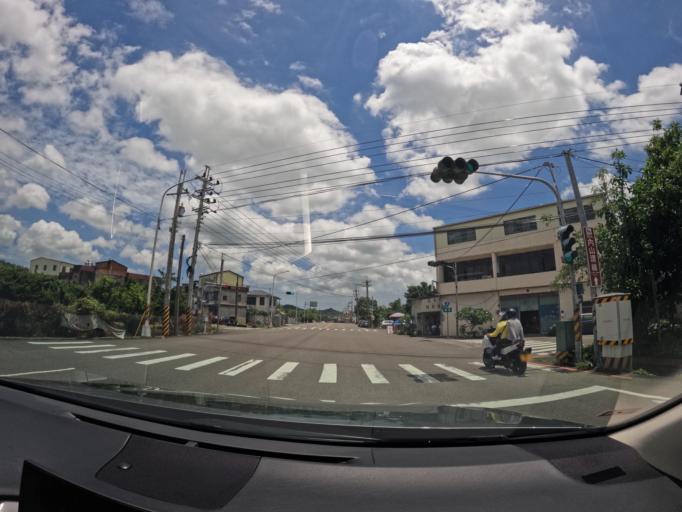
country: TW
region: Taiwan
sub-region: Miaoli
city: Miaoli
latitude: 24.6396
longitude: 120.9559
